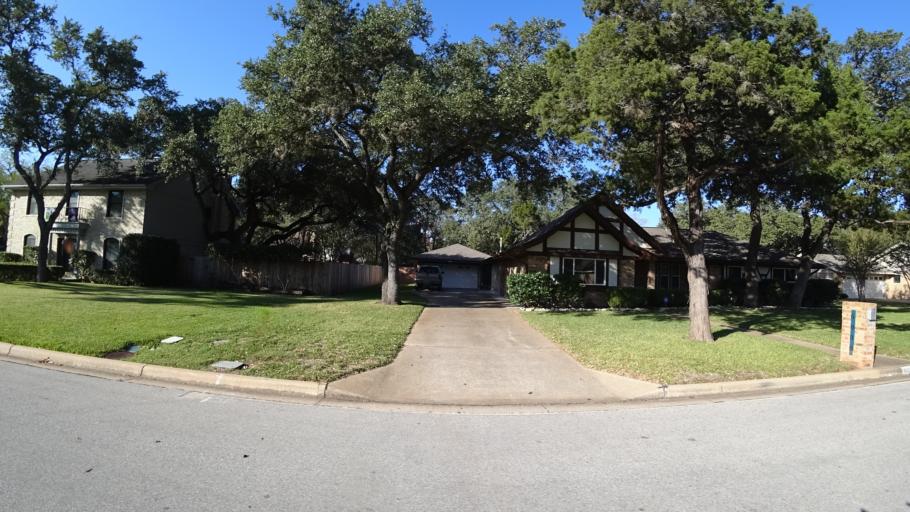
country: US
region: Texas
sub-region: Travis County
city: Shady Hollow
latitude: 30.2221
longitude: -97.8455
